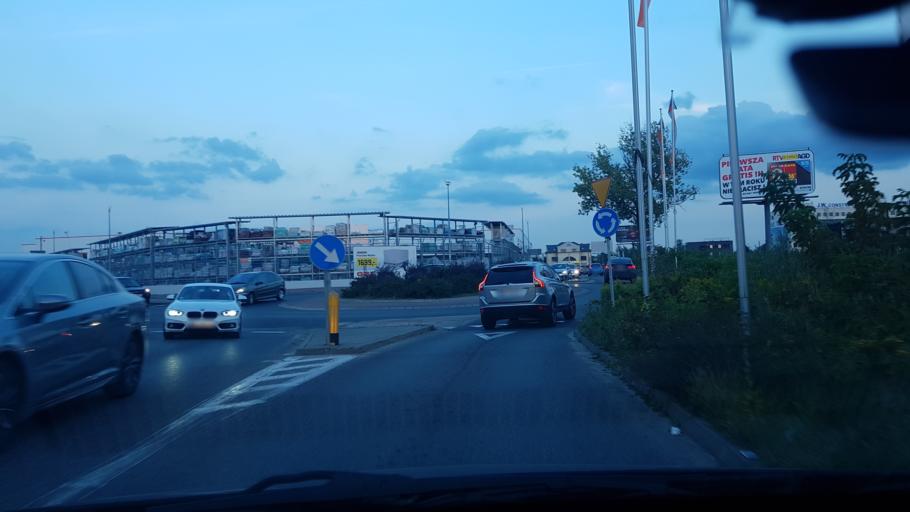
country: PL
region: Masovian Voivodeship
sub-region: Powiat wolominski
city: Zabki
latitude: 52.3029
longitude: 21.0838
